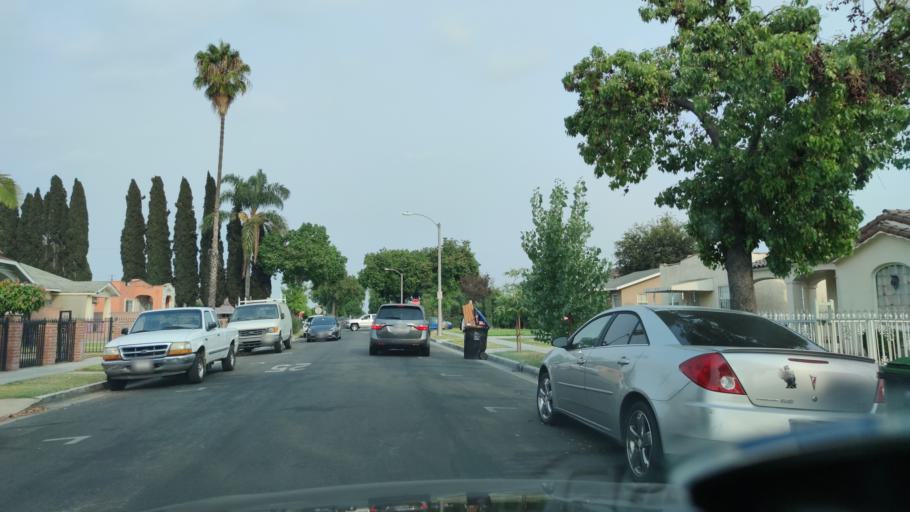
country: US
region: California
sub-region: Los Angeles County
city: Maywood
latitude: 33.9893
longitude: -118.1972
